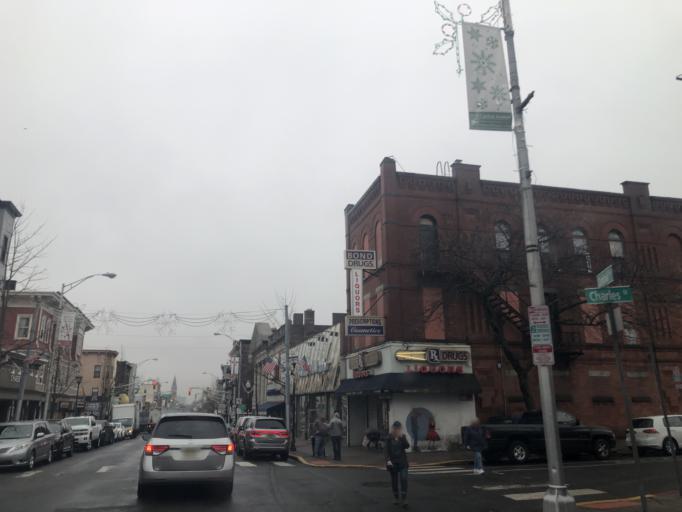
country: US
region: New Jersey
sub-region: Hudson County
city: Hoboken
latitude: 40.7481
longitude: -74.0479
